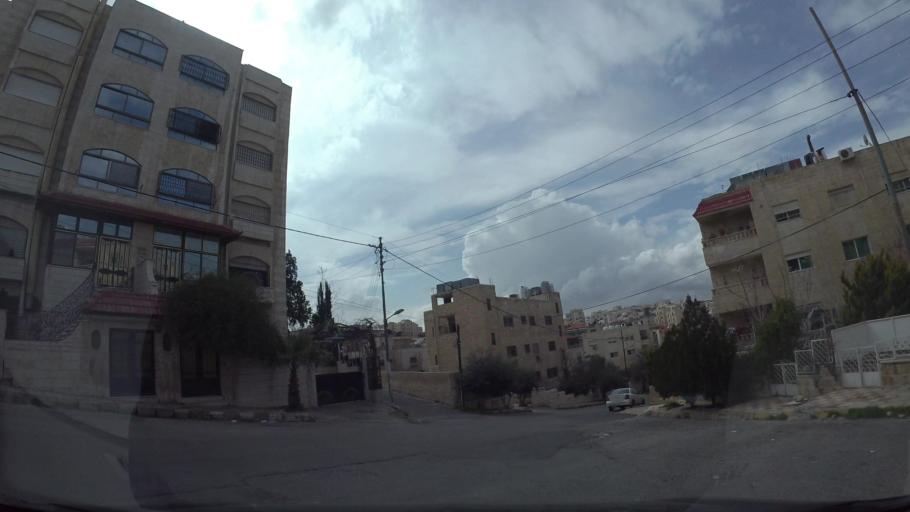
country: JO
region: Amman
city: Amman
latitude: 32.0023
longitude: 35.9377
